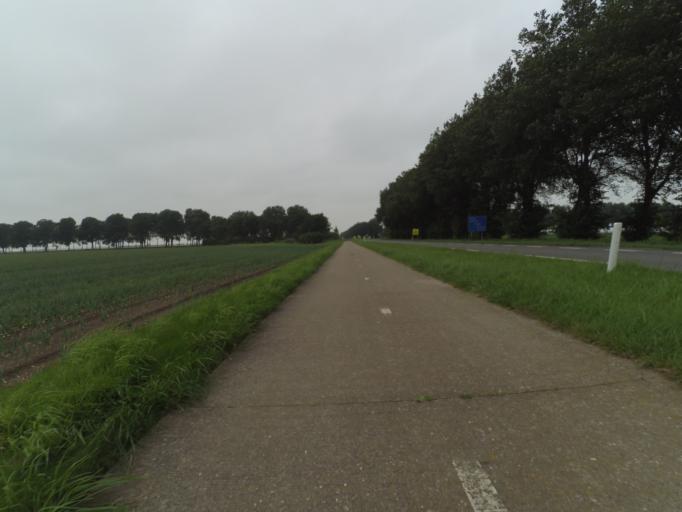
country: NL
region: Flevoland
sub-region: Gemeente Zeewolde
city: Zeewolde
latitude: 52.3869
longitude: 5.4425
